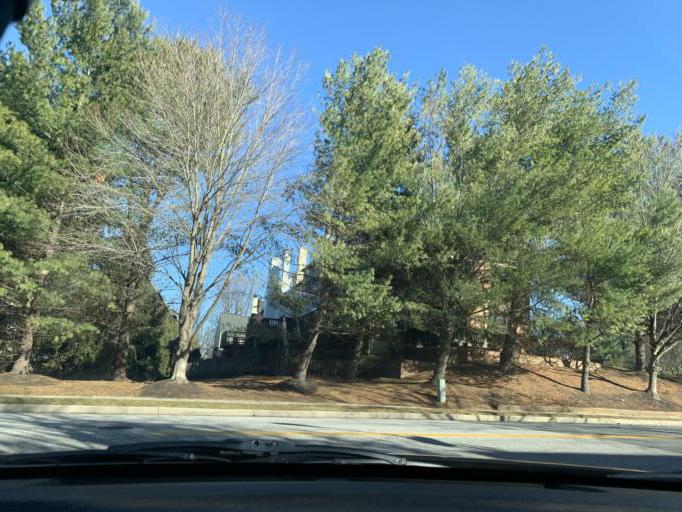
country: US
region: Maryland
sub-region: Baltimore County
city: Garrison
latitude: 39.3971
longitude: -76.7559
